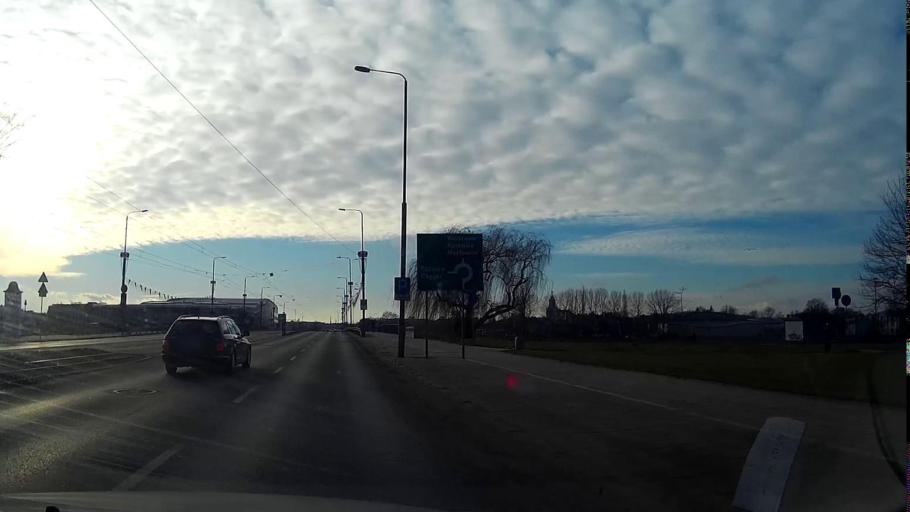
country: PL
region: Lesser Poland Voivodeship
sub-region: Krakow
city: Krakow
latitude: 50.0503
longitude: 19.9361
